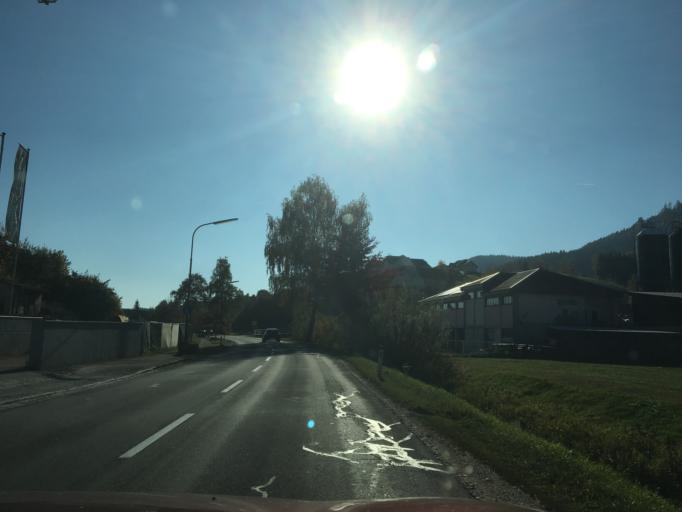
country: AT
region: Upper Austria
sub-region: Politischer Bezirk Perg
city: Sankt Georgen am Walde
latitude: 48.4368
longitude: 14.7807
